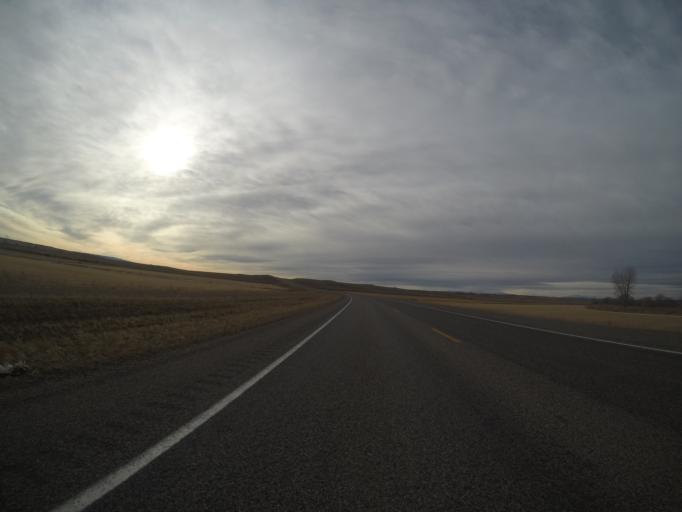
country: US
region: Montana
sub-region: Yellowstone County
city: Laurel
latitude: 45.6123
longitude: -108.8205
